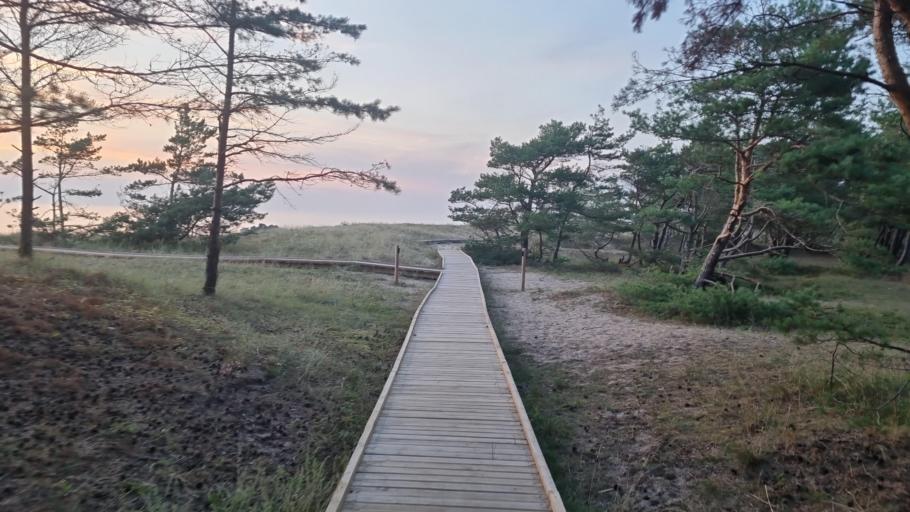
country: LV
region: Ventspils
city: Ventspils
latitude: 57.2471
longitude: 21.4145
